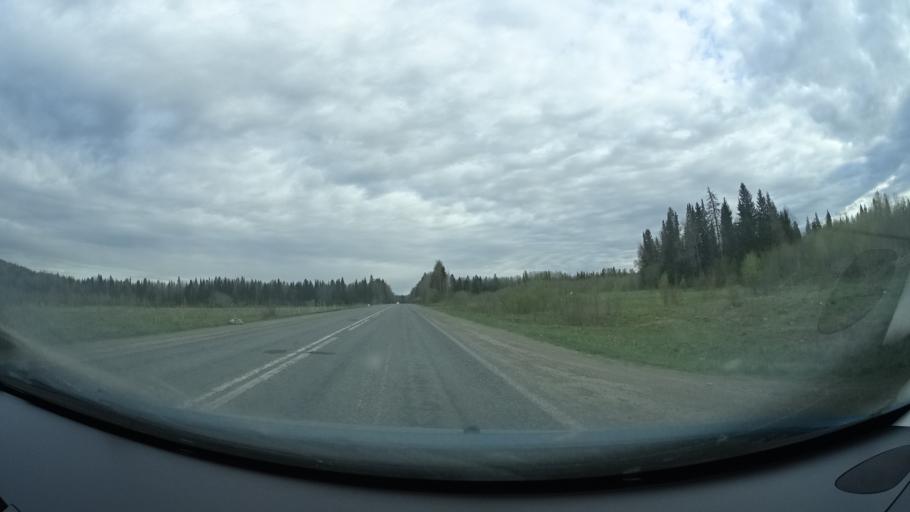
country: RU
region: Perm
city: Yugo-Kamskiy
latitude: 57.6714
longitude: 55.5847
